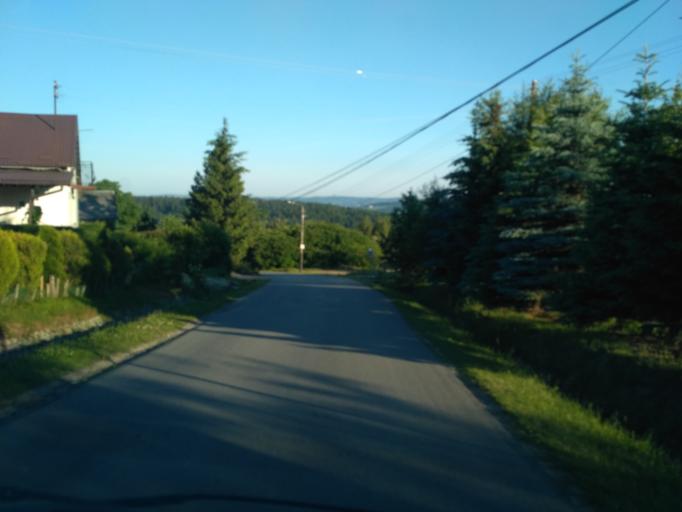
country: PL
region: Subcarpathian Voivodeship
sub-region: Powiat rzeszowski
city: Lubenia
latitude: 49.9223
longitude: 21.9114
